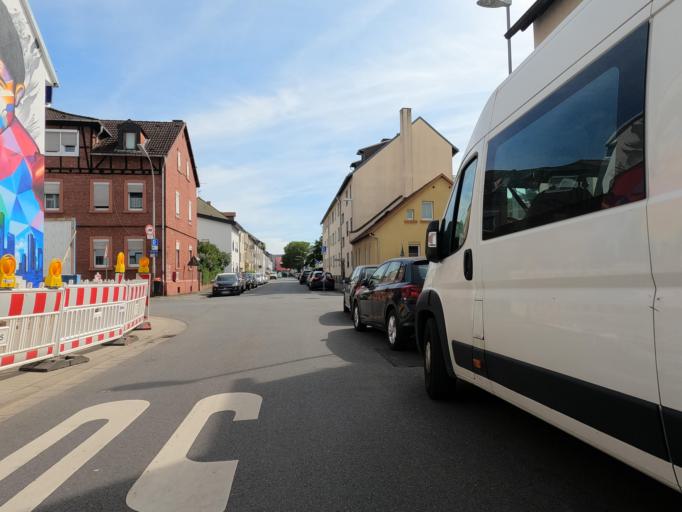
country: DE
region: Hesse
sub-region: Regierungsbezirk Darmstadt
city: Neu Isenburg
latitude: 50.0520
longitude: 8.6975
